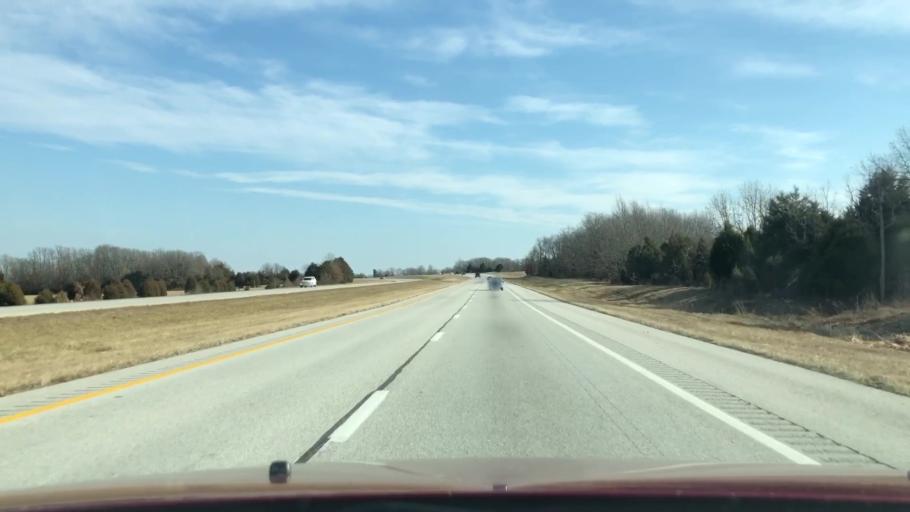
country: US
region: Missouri
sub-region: Webster County
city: Seymour
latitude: 37.1646
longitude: -92.8789
